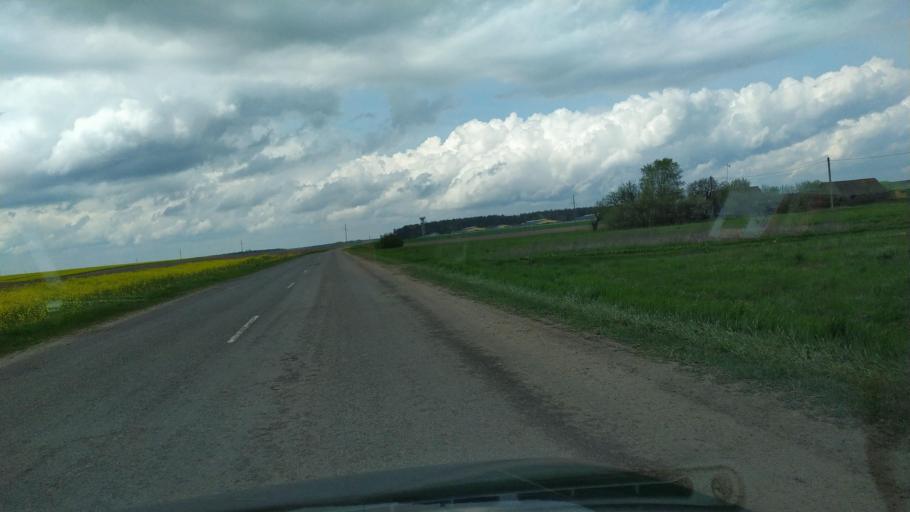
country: BY
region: Brest
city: Pruzhany
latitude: 52.6343
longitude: 24.3850
